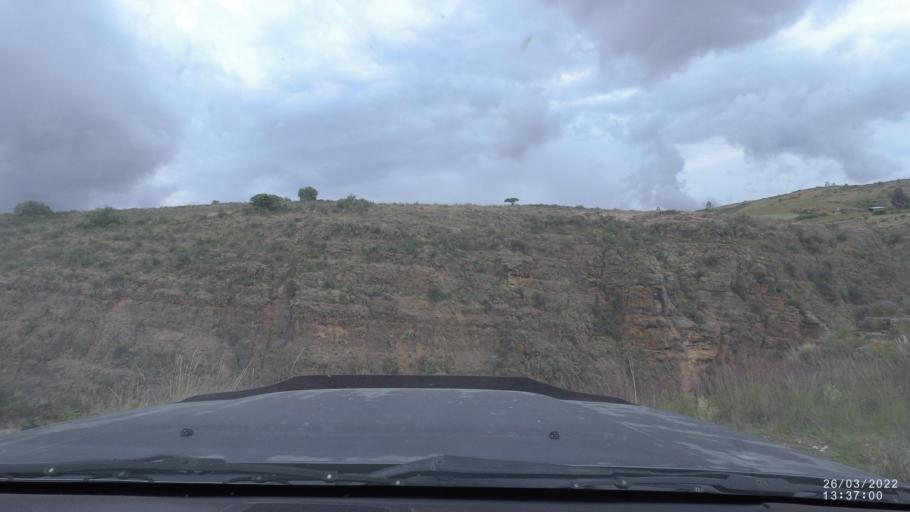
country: BO
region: Cochabamba
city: Cliza
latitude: -17.7435
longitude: -65.8687
